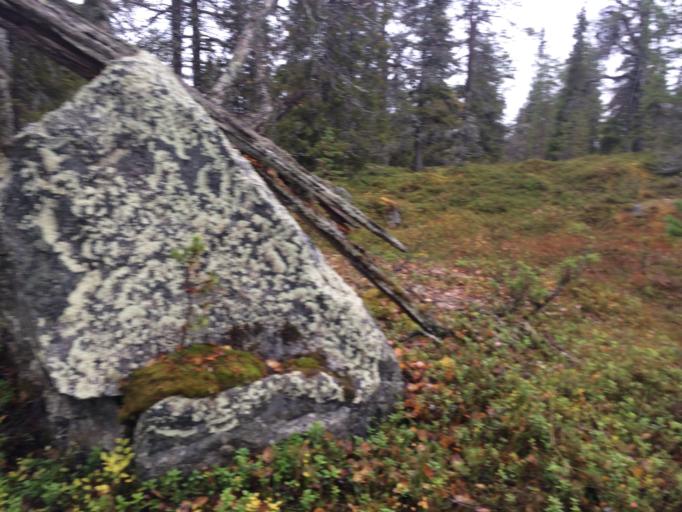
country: FI
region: Lapland
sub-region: Itae-Lappi
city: Posio
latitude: 65.9744
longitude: 28.6080
